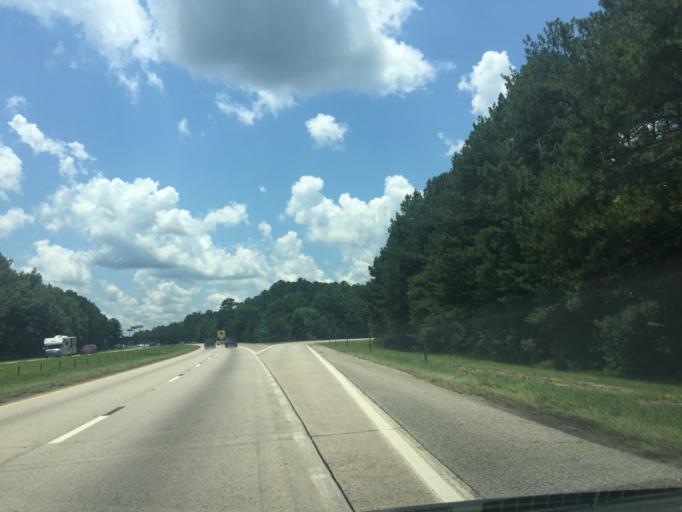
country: US
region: South Carolina
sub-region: Jasper County
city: Ridgeland
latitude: 32.4506
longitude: -80.9917
